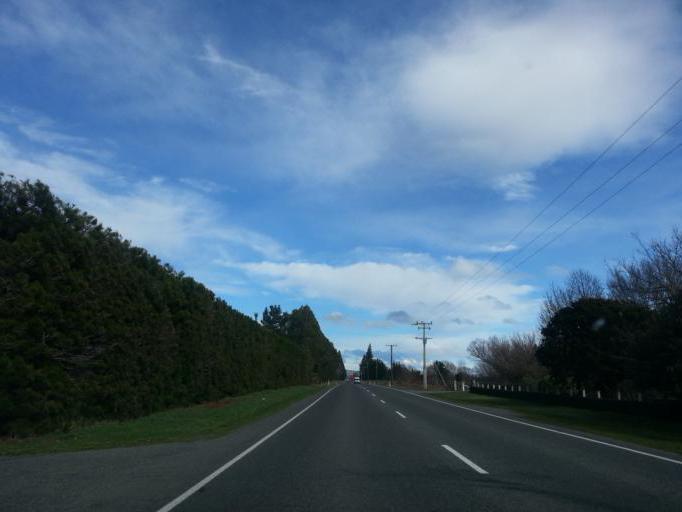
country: NZ
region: Canterbury
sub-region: Hurunui District
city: Amberley
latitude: -42.7870
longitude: 172.8378
